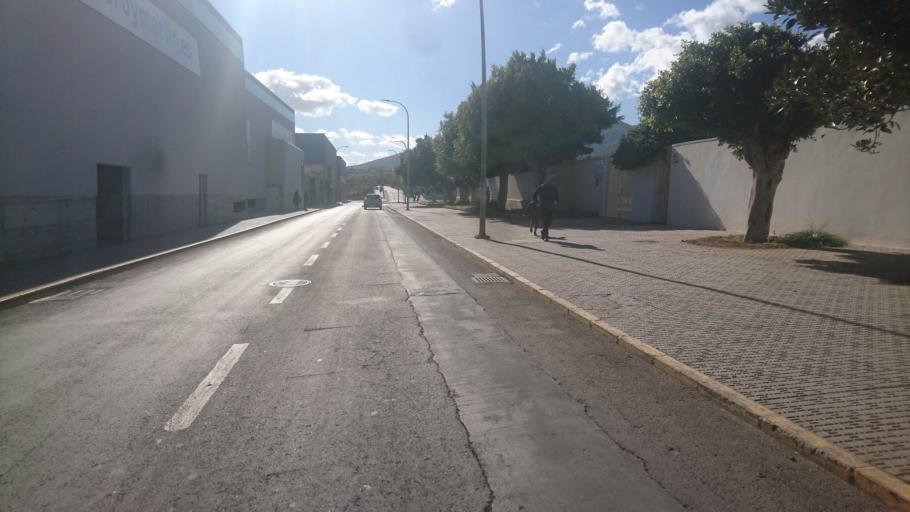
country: ES
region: Melilla
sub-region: Melilla
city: Melilla
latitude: 35.2710
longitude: -2.9400
